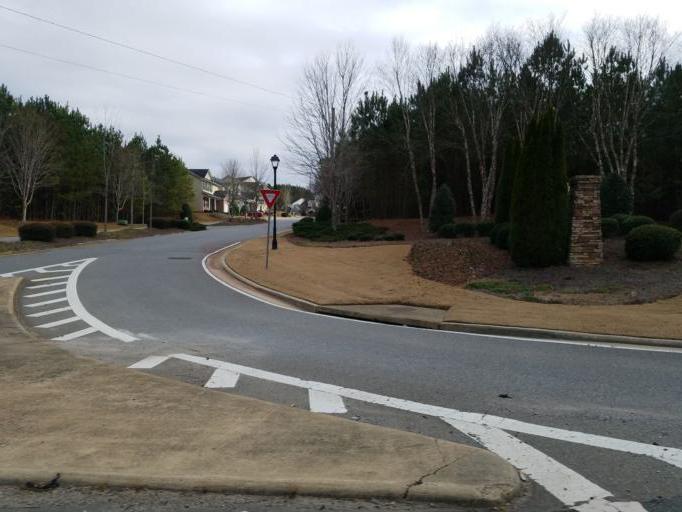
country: US
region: Georgia
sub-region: Cherokee County
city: Canton
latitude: 34.2163
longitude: -84.5157
